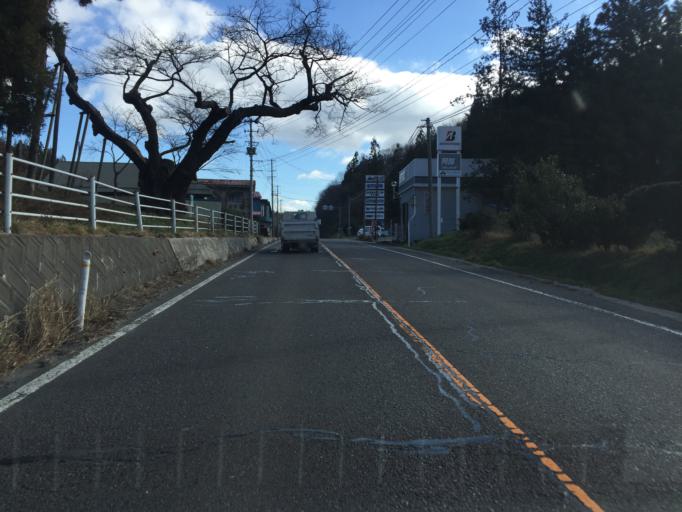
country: JP
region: Fukushima
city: Ishikawa
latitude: 37.2315
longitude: 140.5782
